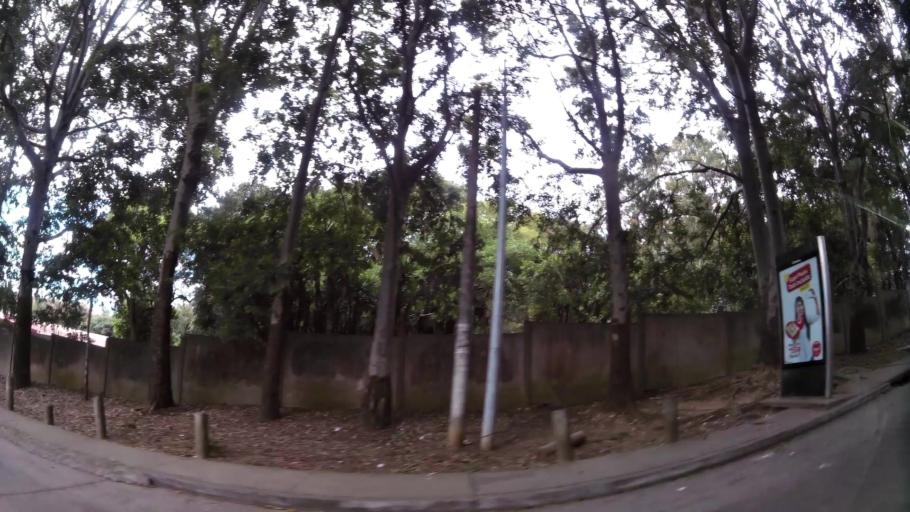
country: GT
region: Guatemala
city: Santa Catarina Pinula
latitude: 14.5705
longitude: -90.5355
